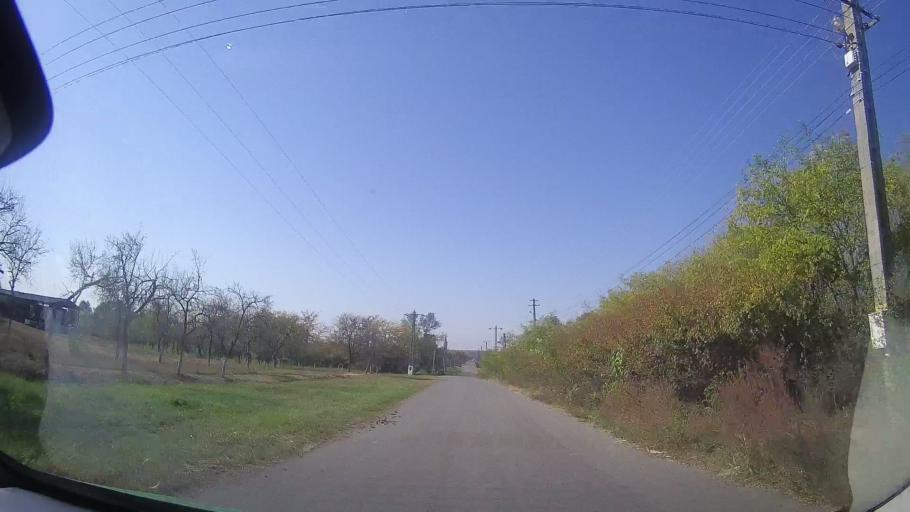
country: RO
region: Timis
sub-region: Comuna Ghizela
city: Ghizela
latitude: 45.8245
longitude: 21.7512
